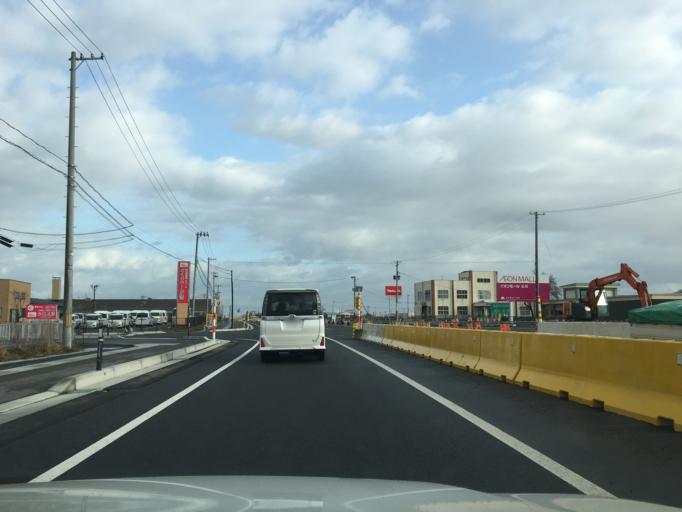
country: JP
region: Yamagata
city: Sakata
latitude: 38.8481
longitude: 139.8486
